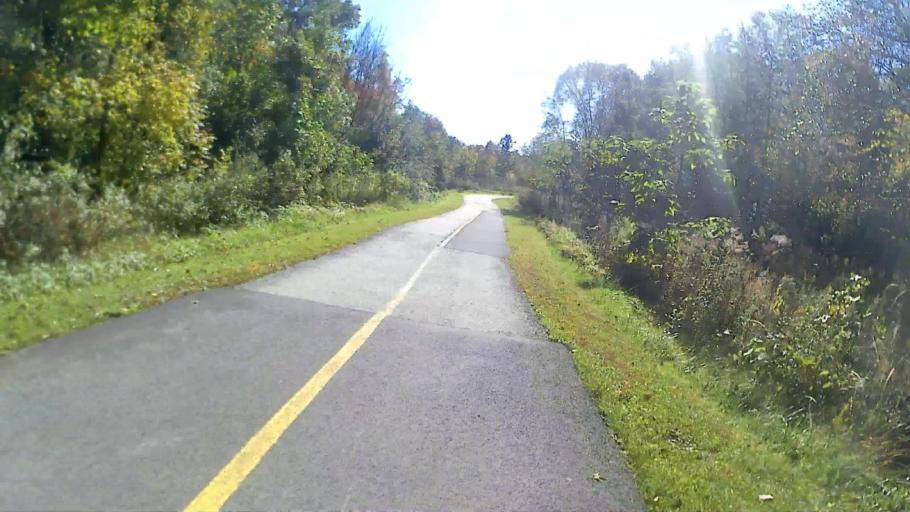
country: US
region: Illinois
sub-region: Cook County
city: Elk Grove Village
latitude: 42.0166
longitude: -87.9984
